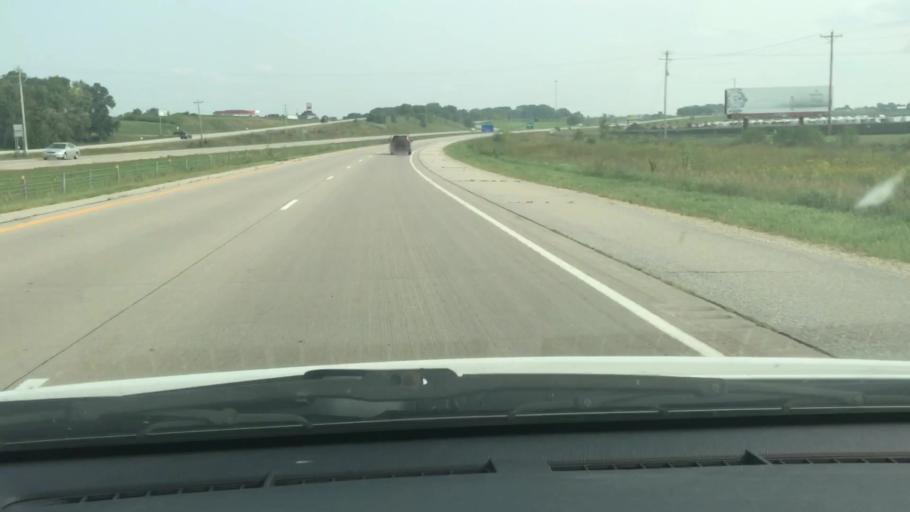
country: US
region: Minnesota
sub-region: Olmsted County
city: Oronoco
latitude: 44.1531
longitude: -92.5328
